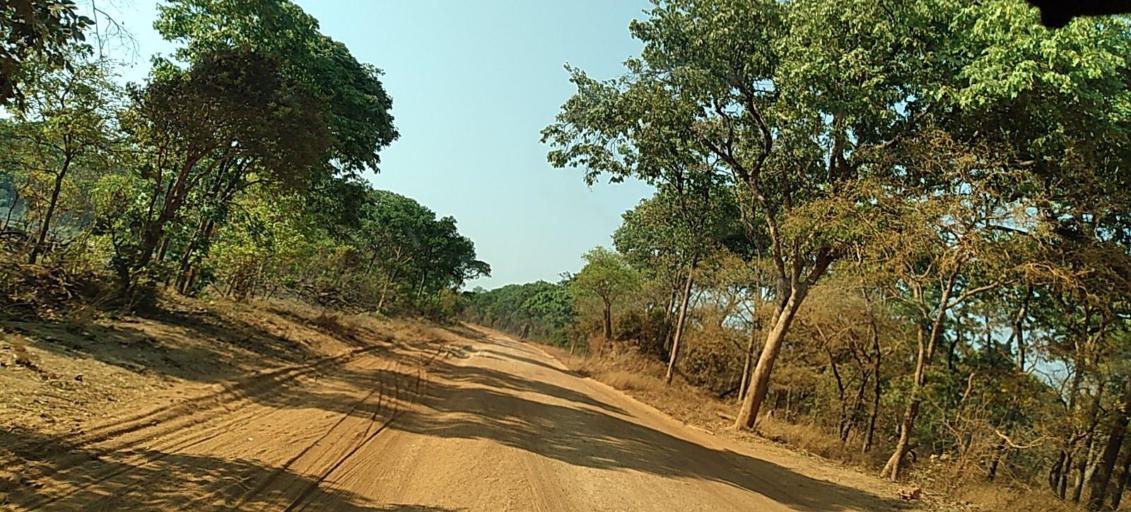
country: ZM
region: North-Western
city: Kasempa
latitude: -13.6602
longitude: 26.0097
